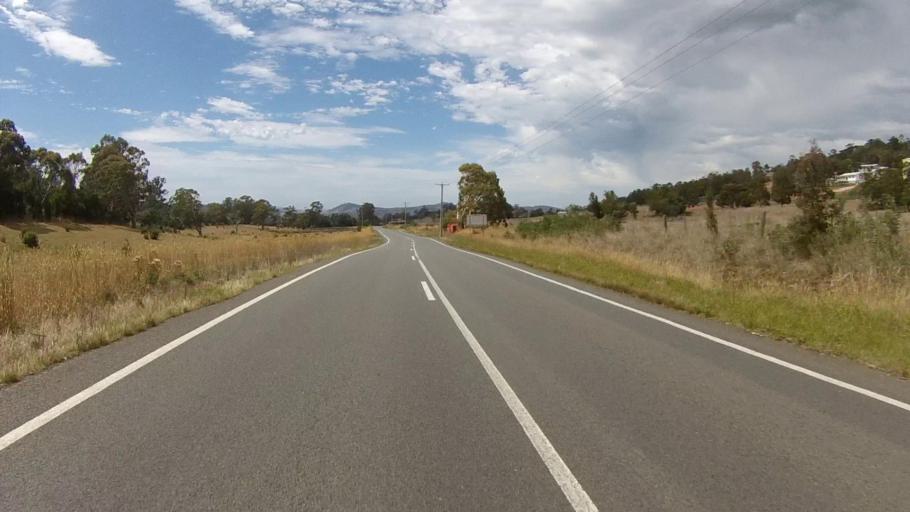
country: AU
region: Tasmania
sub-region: Brighton
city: Old Beach
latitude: -42.6717
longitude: 147.3920
